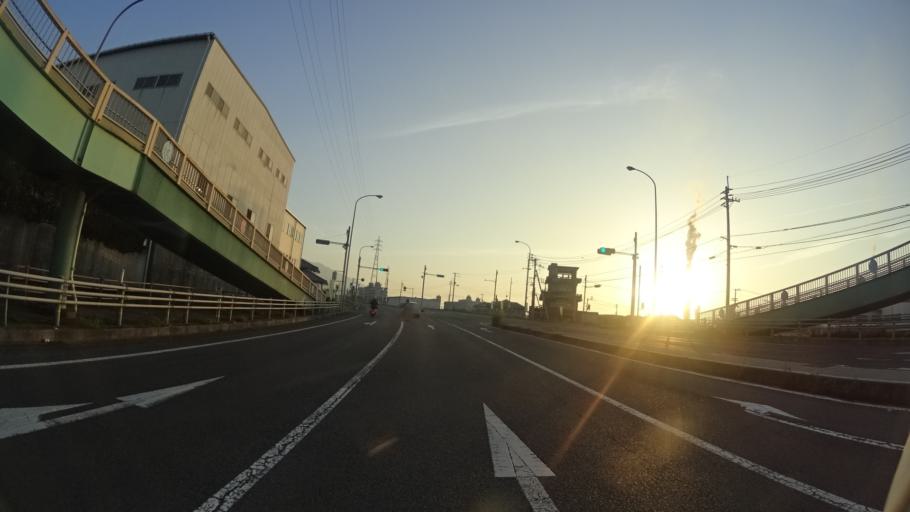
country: JP
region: Ehime
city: Kawanoecho
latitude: 33.9874
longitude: 133.5631
